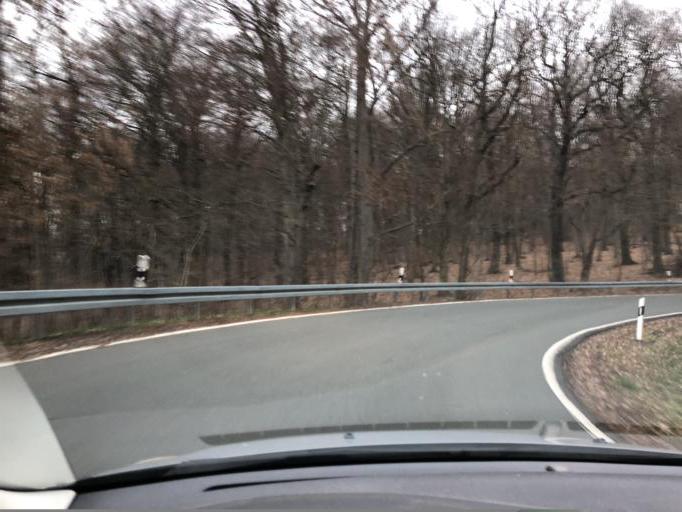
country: DE
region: Saxony-Anhalt
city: Bad Bibra
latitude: 51.1722
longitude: 11.6124
